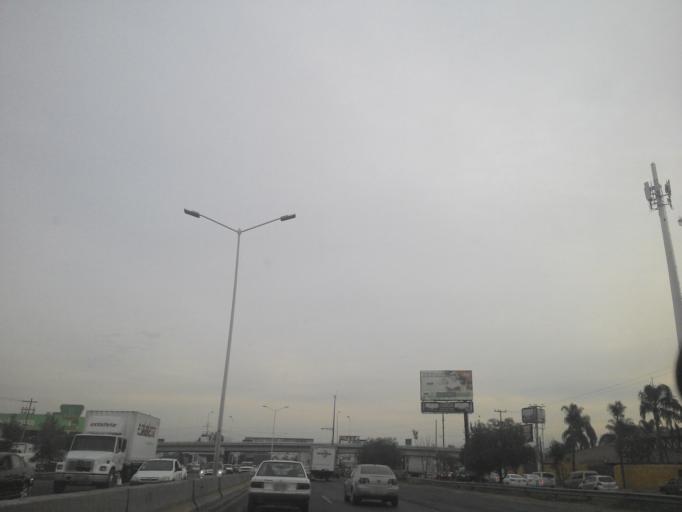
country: MX
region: Jalisco
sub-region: Tlajomulco de Zuniga
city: Palomar
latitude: 20.6324
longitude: -103.4368
